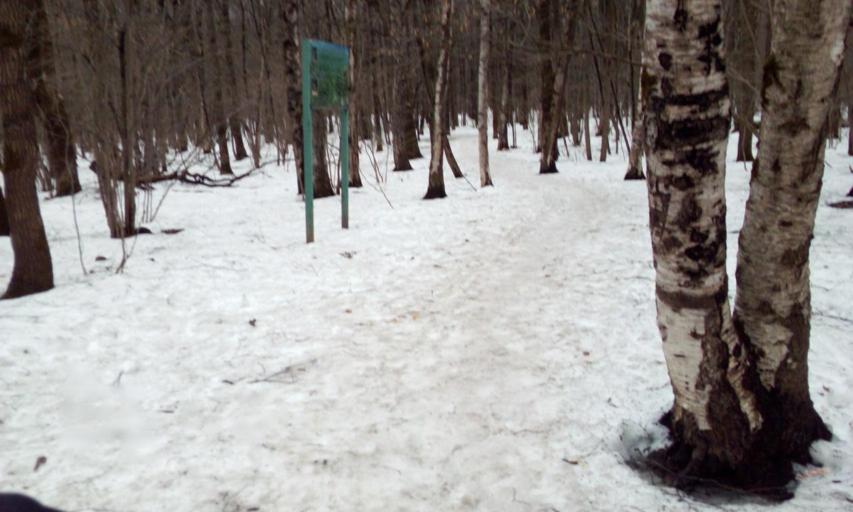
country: RU
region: Moscow
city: Troparevo
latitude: 55.6380
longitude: 37.4834
